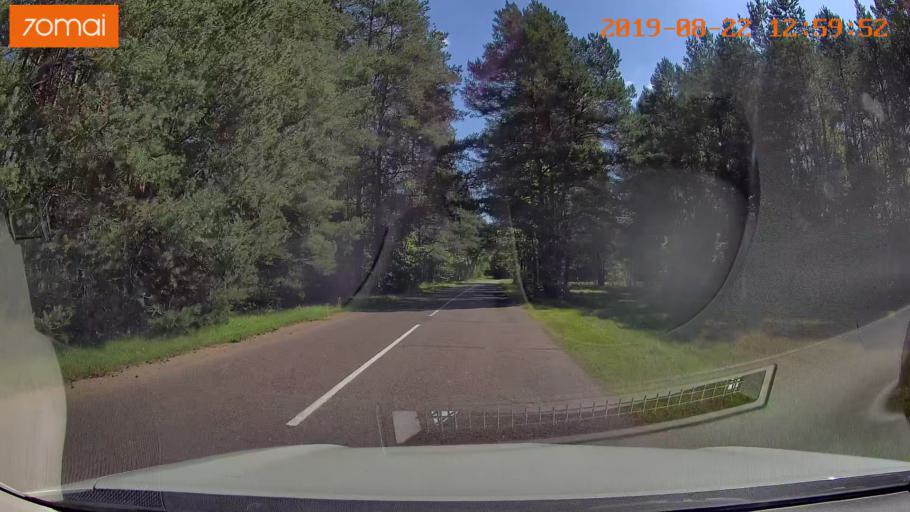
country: BY
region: Minsk
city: Prawdzinski
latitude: 53.4211
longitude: 27.7999
